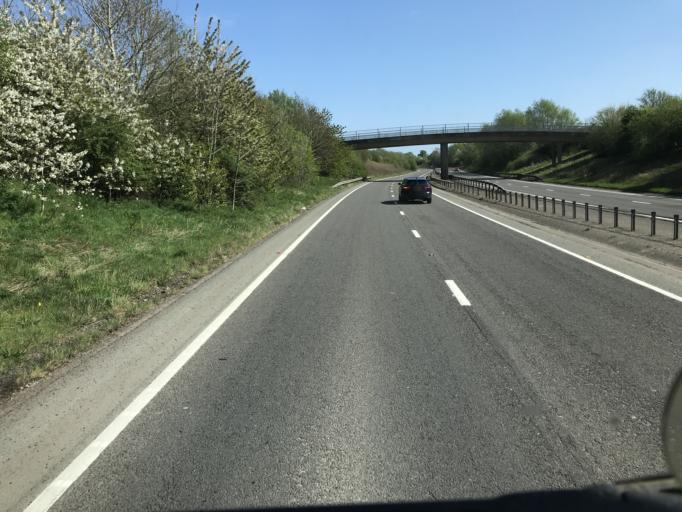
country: GB
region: England
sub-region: Cheshire East
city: Weston
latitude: 53.0714
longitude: -2.3961
